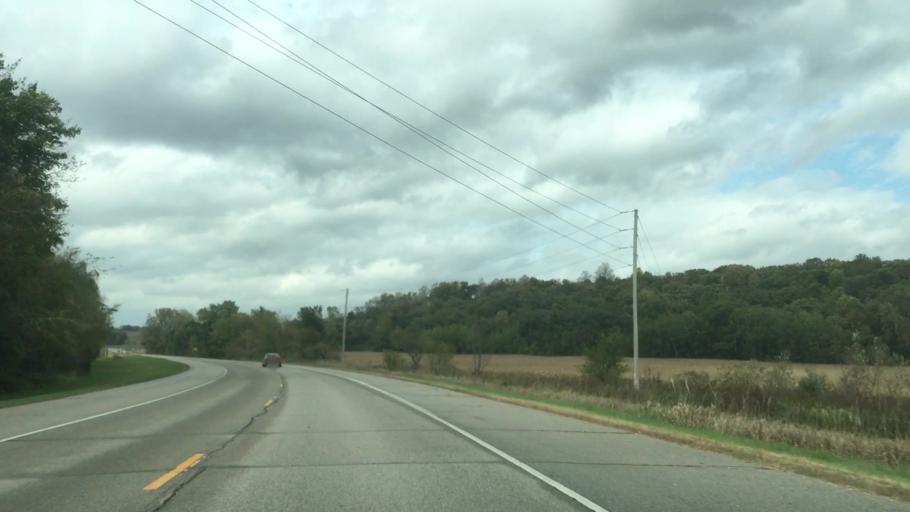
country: US
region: Minnesota
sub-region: Fillmore County
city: Chatfield
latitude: 43.8930
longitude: -92.2290
